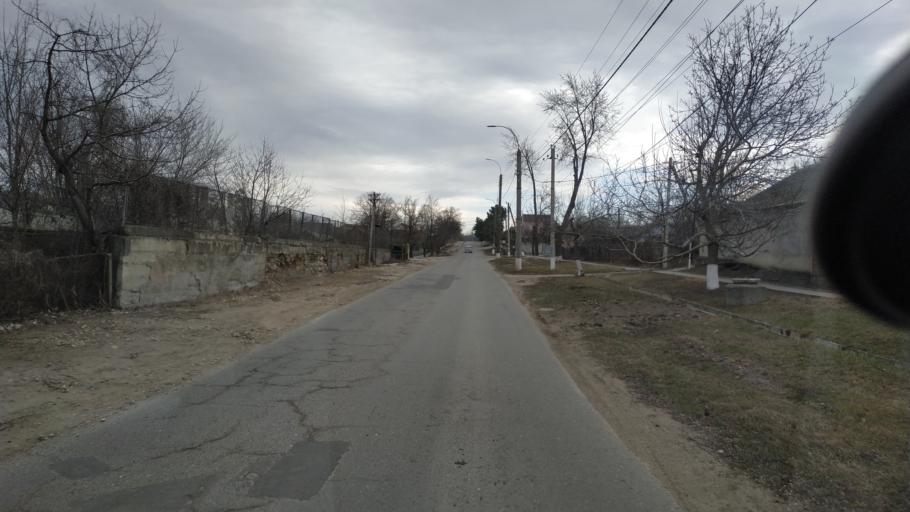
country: MD
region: Chisinau
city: Vadul lui Voda
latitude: 47.0973
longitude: 29.0705
